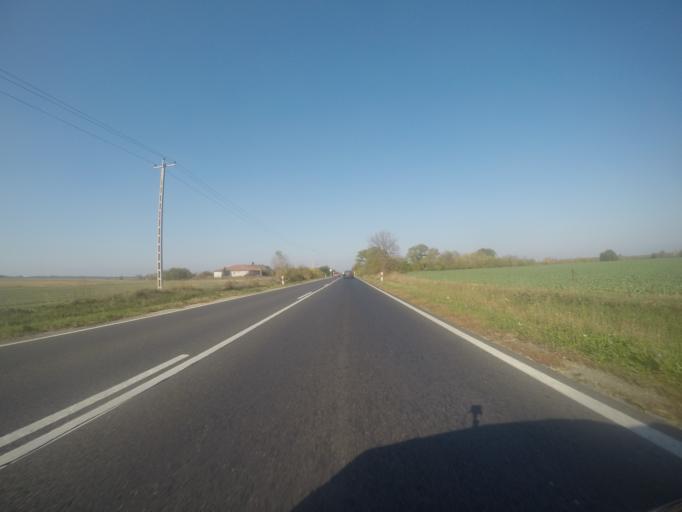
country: HU
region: Fejer
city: Baracs
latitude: 46.8485
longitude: 18.9114
